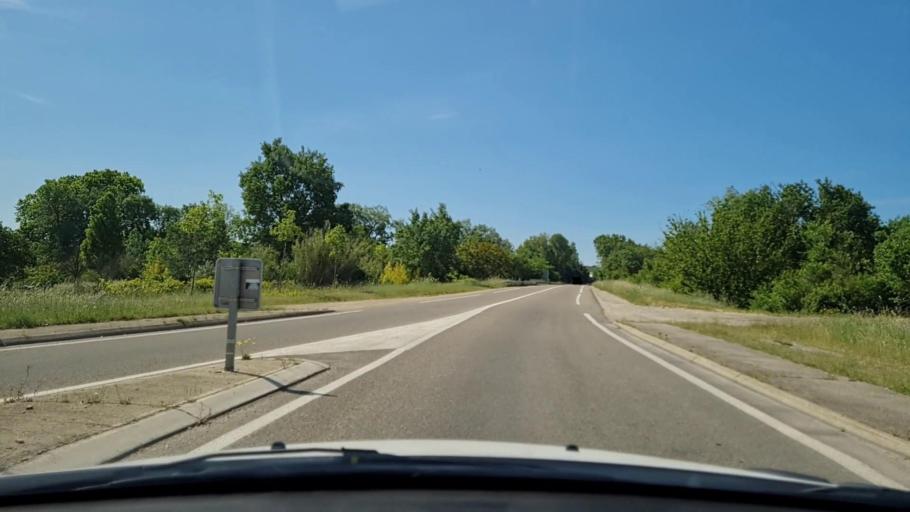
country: FR
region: Languedoc-Roussillon
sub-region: Departement du Gard
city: La Calmette
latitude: 43.9327
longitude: 4.2565
